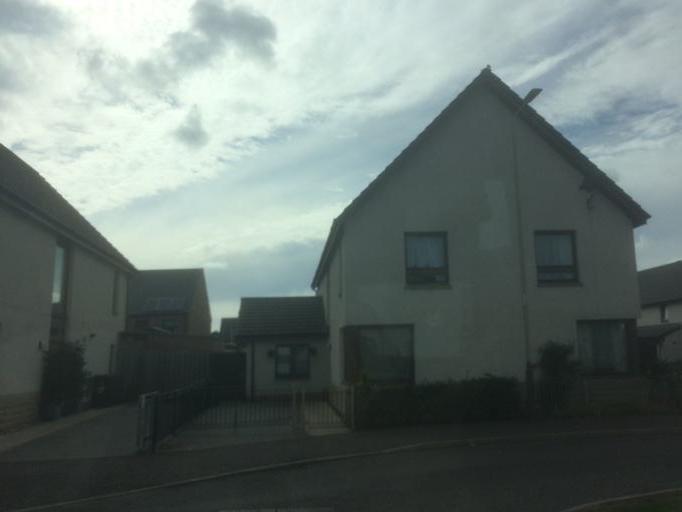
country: GB
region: Scotland
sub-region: Perth and Kinross
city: Perth
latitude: 56.4088
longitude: -3.4415
